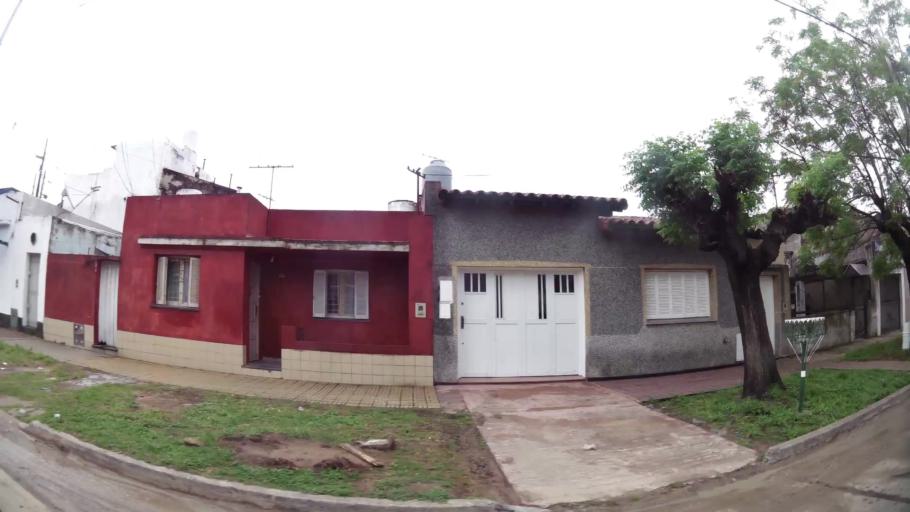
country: AR
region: Buenos Aires
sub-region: Partido de Lanus
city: Lanus
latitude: -34.7296
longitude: -58.3850
